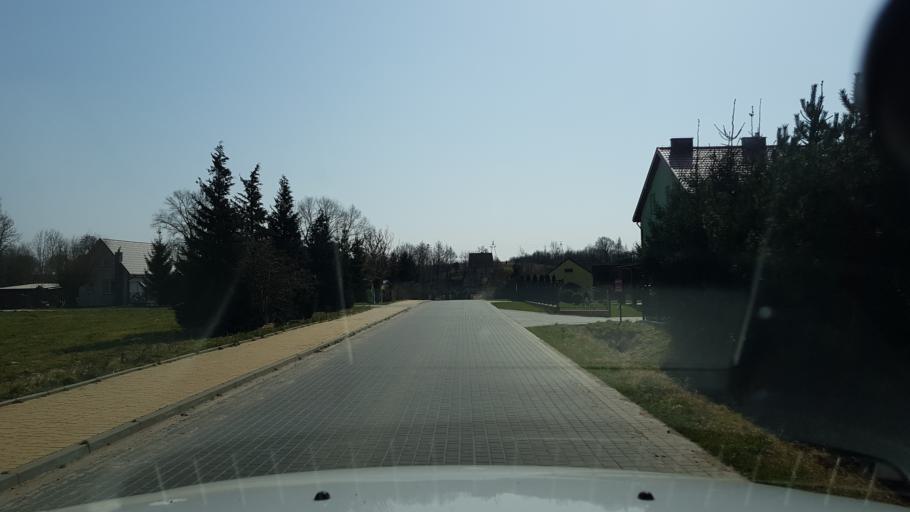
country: PL
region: West Pomeranian Voivodeship
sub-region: Powiat slawienski
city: Darlowo
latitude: 54.5089
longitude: 16.5020
